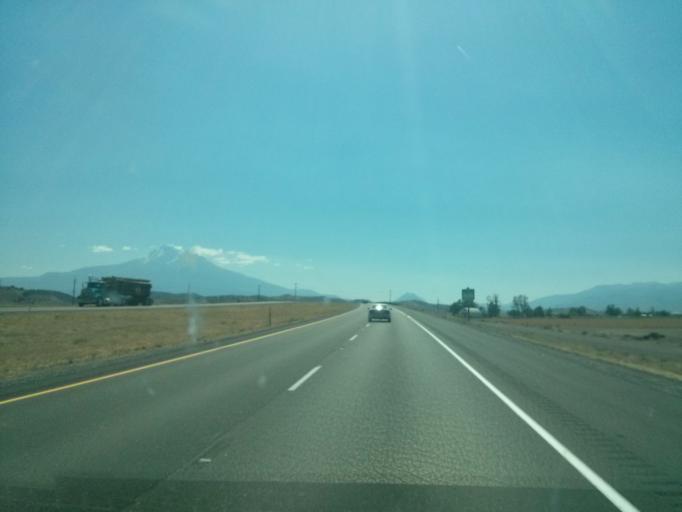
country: US
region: California
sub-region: Siskiyou County
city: Montague
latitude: 41.6311
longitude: -122.5248
